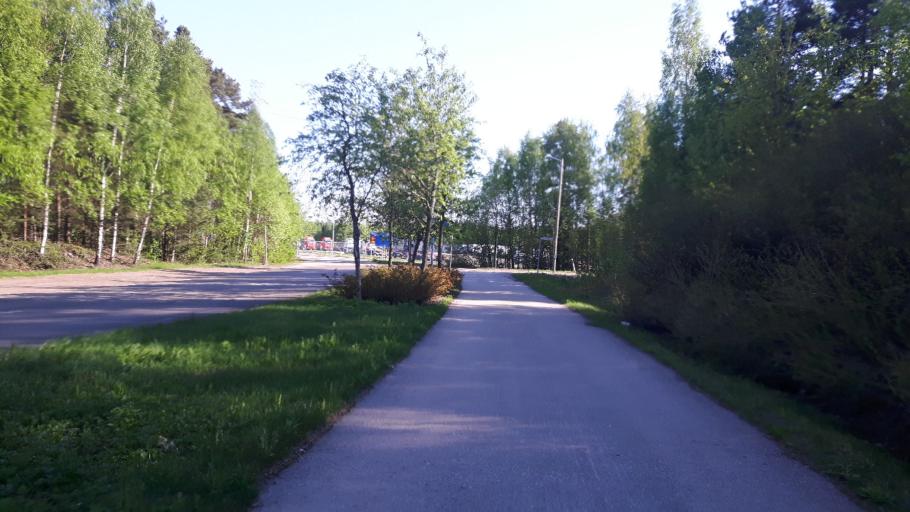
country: FI
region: Kymenlaakso
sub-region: Kotka-Hamina
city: Kotka
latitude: 60.4365
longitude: 26.8813
